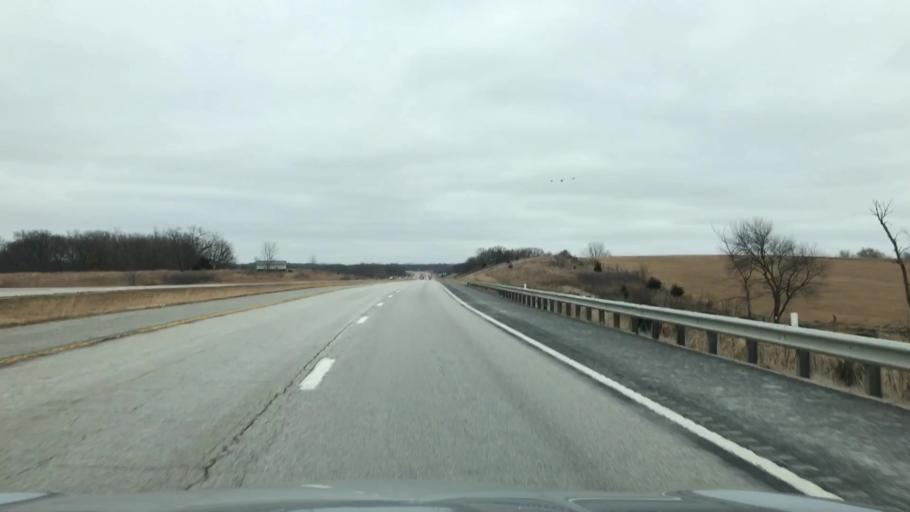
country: US
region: Missouri
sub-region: Caldwell County
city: Hamilton
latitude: 39.7464
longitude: -94.0471
